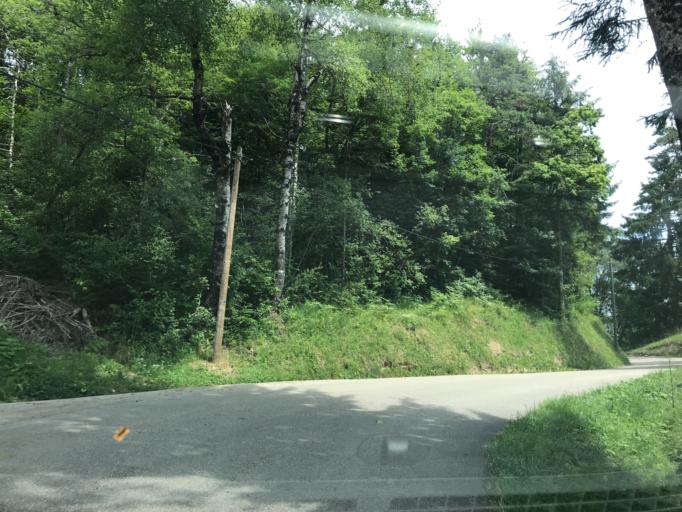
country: FR
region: Rhone-Alpes
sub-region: Departement de l'Isere
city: Barraux
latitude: 45.4141
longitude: 5.9516
